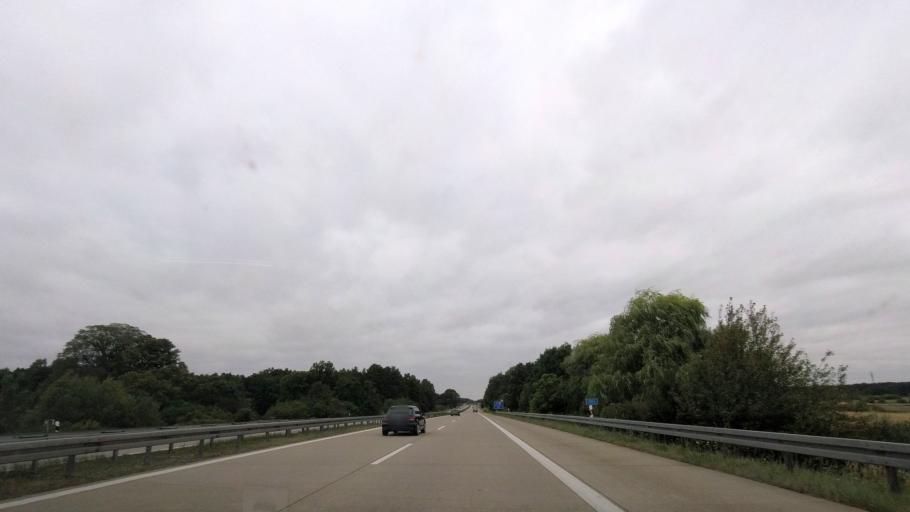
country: DE
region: Brandenburg
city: Althuttendorf
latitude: 53.0828
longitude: 13.8474
